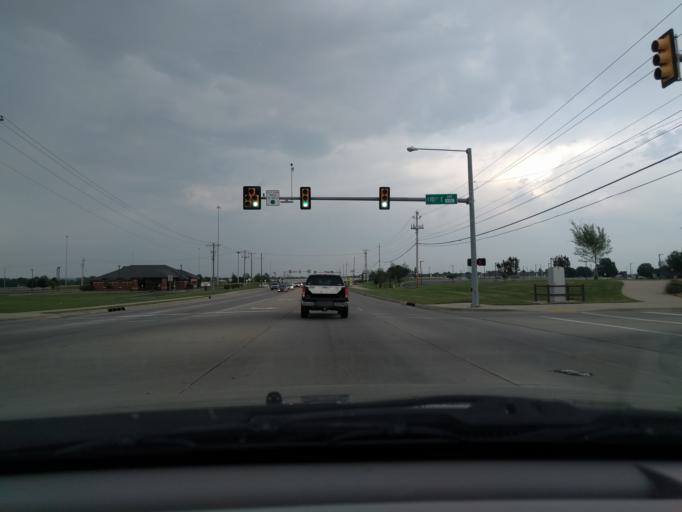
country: US
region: Oklahoma
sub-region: Tulsa County
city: Broken Arrow
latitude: 36.0464
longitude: -95.8645
